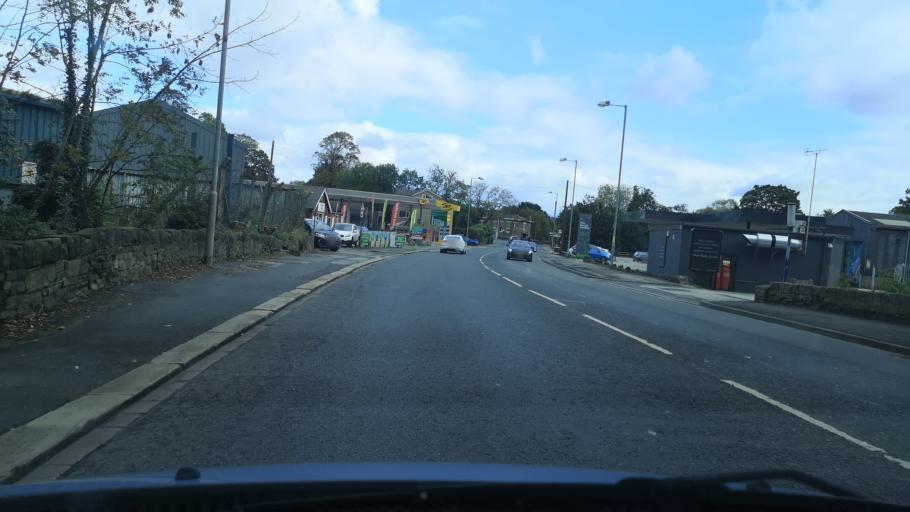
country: GB
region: England
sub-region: City and Borough of Wakefield
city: Middlestown
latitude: 53.6562
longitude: -1.5806
